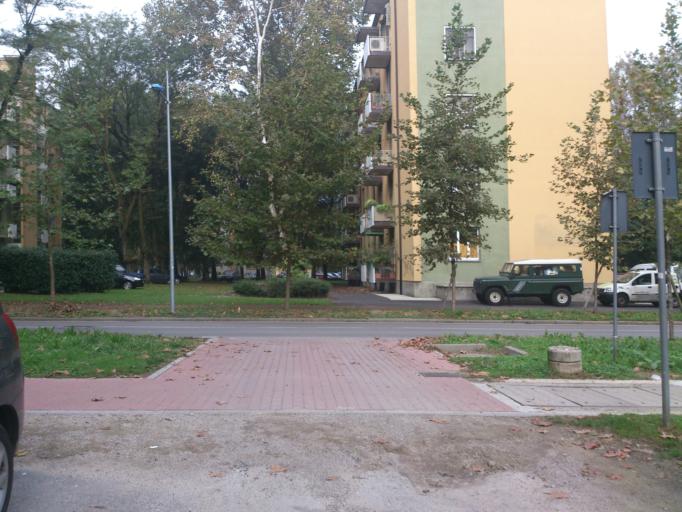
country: IT
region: Lombardy
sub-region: Citta metropolitana di Milano
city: San Donato Milanese
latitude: 45.4237
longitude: 9.2645
